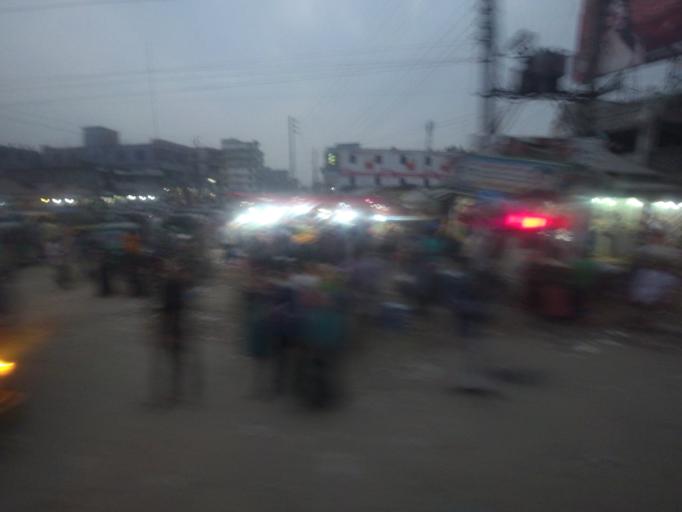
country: BD
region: Dhaka
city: Tangail
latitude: 24.3349
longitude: 89.9248
